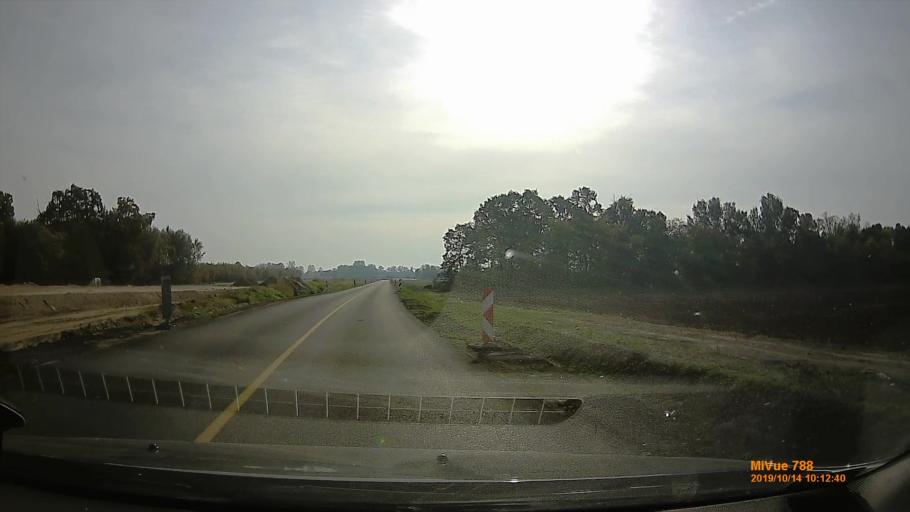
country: HU
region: Pest
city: Tortel
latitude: 47.1901
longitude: 19.9195
